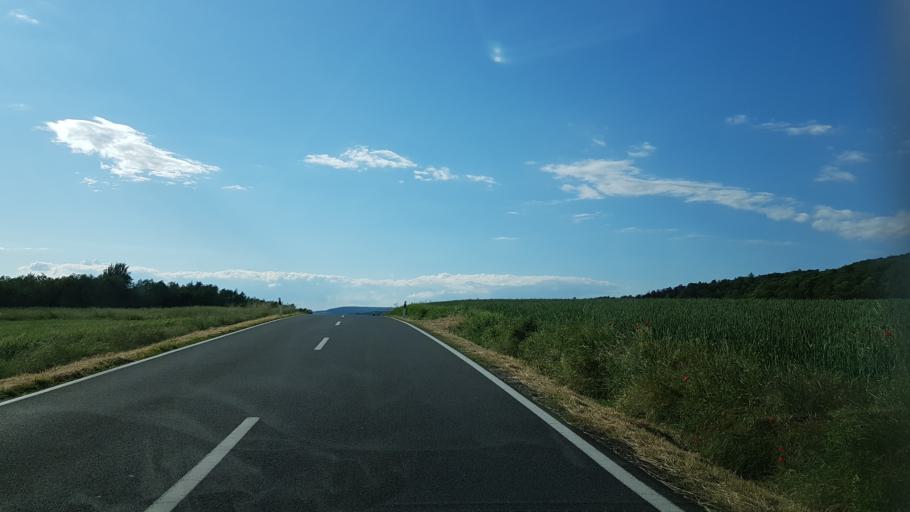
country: DE
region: Lower Saxony
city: Delligsen
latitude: 51.9633
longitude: 9.7729
